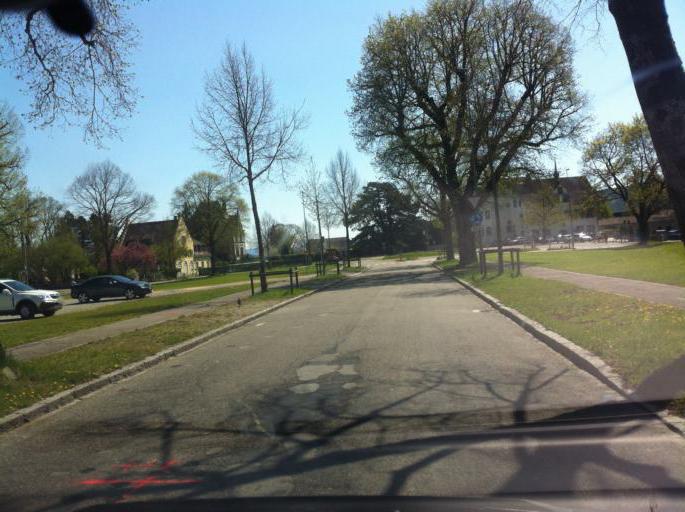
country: CH
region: Schaffhausen
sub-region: Bezirk Schaffhausen
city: Schaffhausen
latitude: 47.7009
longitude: 8.6251
